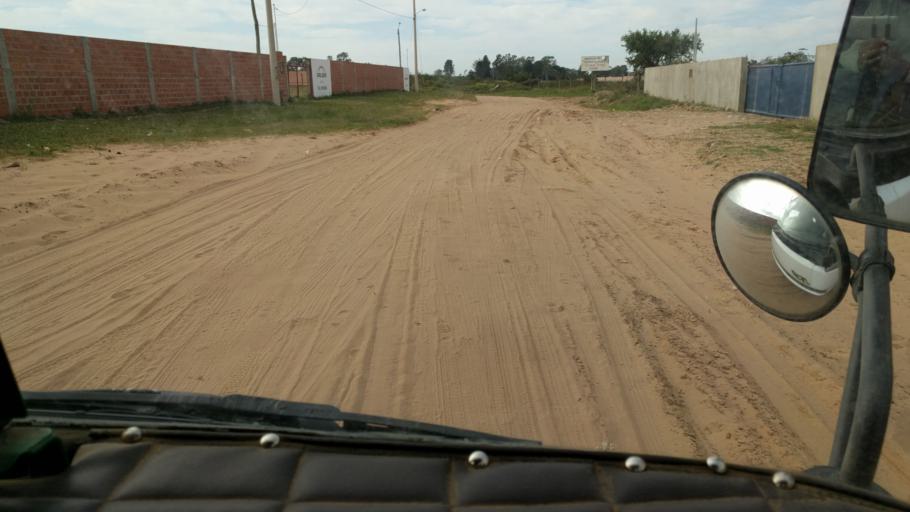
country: BO
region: Santa Cruz
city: Santa Cruz de la Sierra
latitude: -17.6876
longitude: -63.1445
